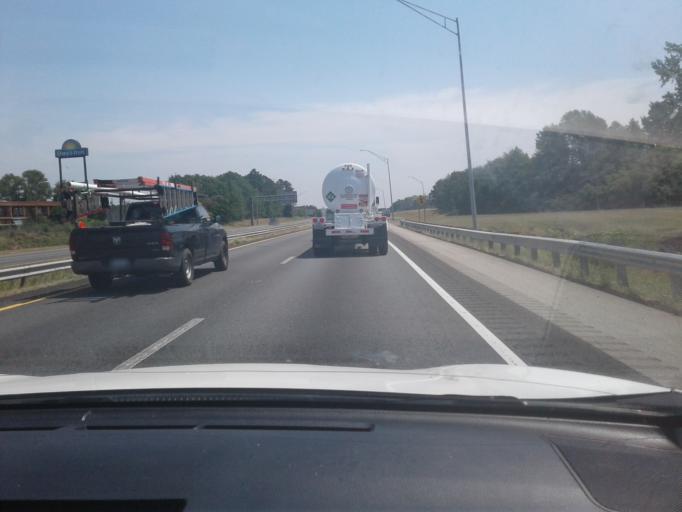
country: US
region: North Carolina
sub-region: Johnston County
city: Benson
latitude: 35.3773
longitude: -78.5385
